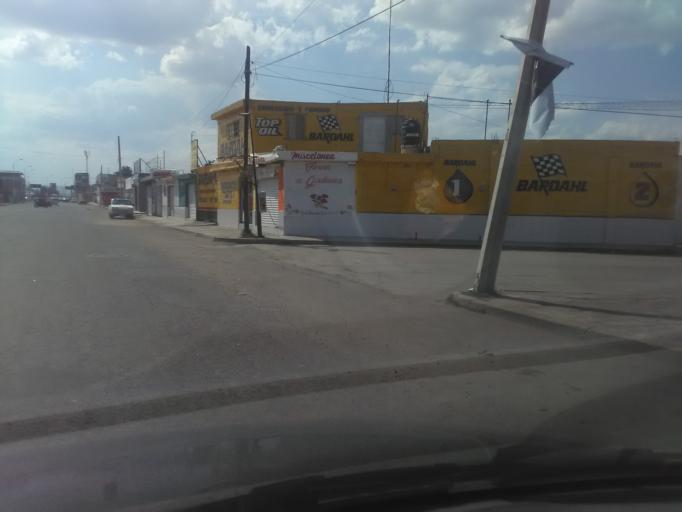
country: MX
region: Durango
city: Victoria de Durango
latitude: 24.0078
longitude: -104.6416
